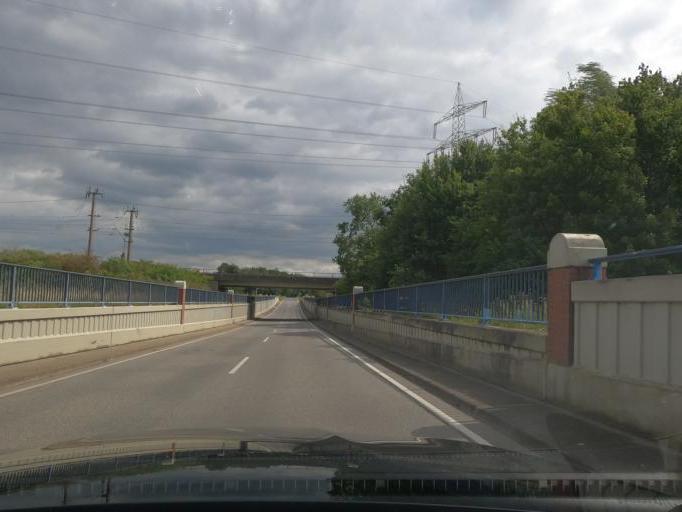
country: DE
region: Lower Saxony
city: Lehrte
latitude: 52.3595
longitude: 10.0131
